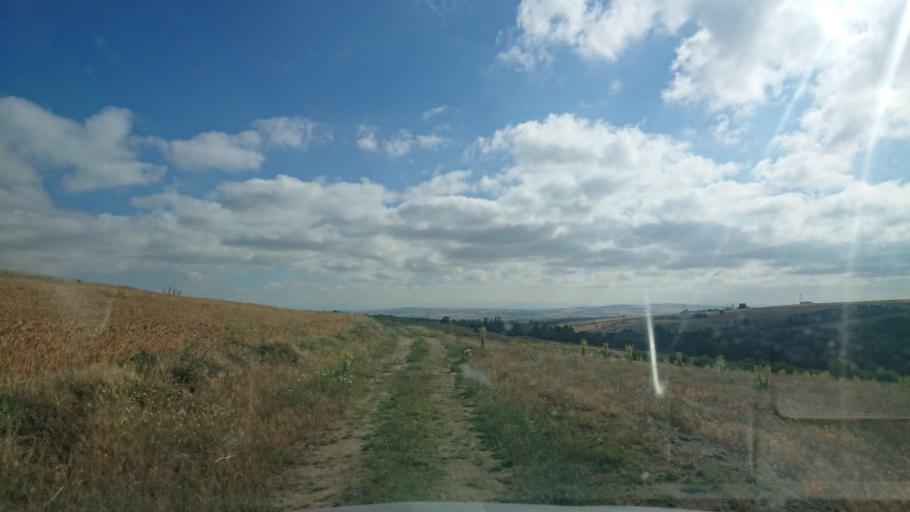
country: TR
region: Aksaray
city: Agacoren
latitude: 38.8493
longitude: 33.9278
